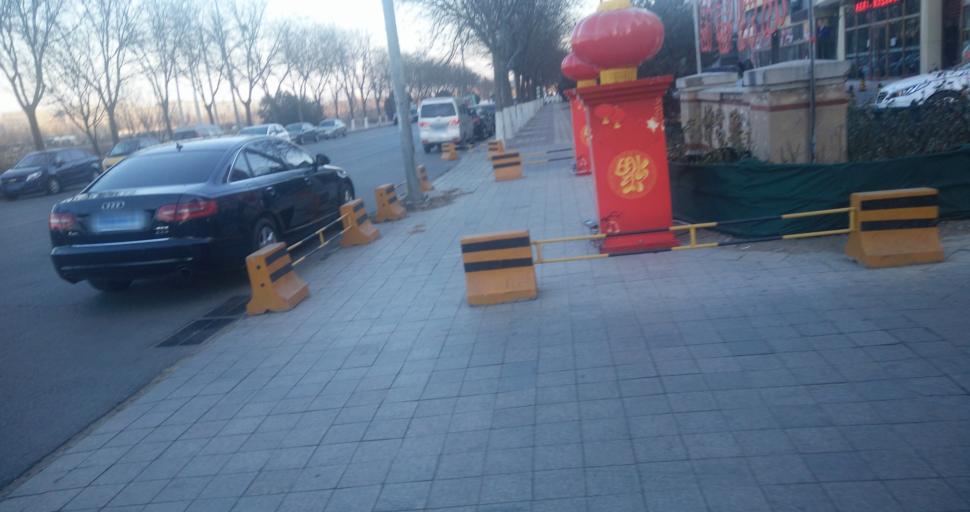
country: CN
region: Beijing
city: Yinghai
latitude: 39.7584
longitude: 116.4979
